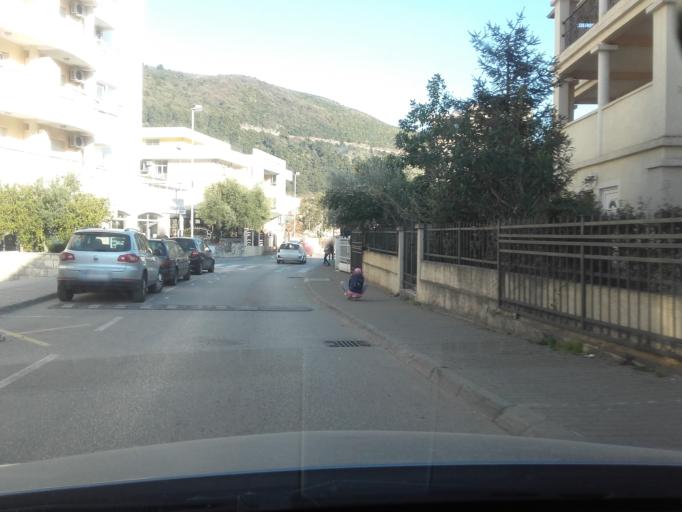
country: ME
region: Budva
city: Budva
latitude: 42.2930
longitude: 18.8441
